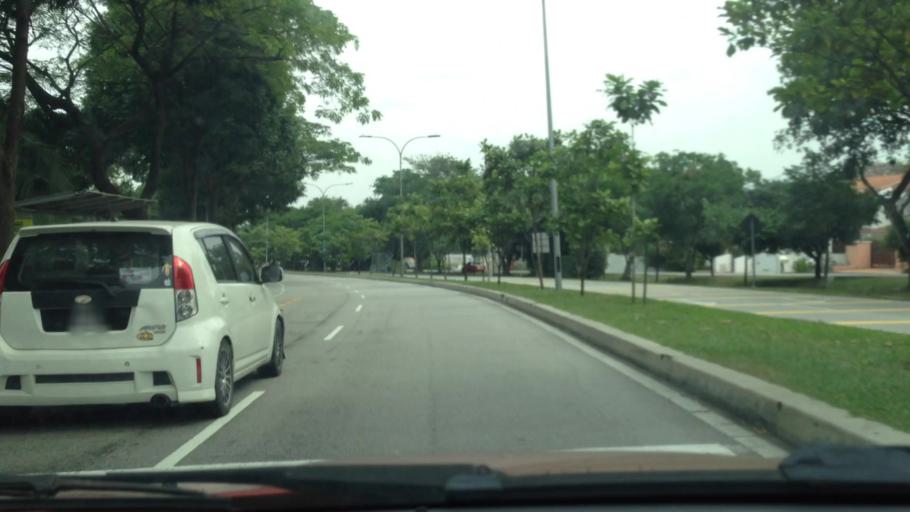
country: MY
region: Selangor
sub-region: Petaling
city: Petaling Jaya
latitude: 3.1012
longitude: 101.6074
